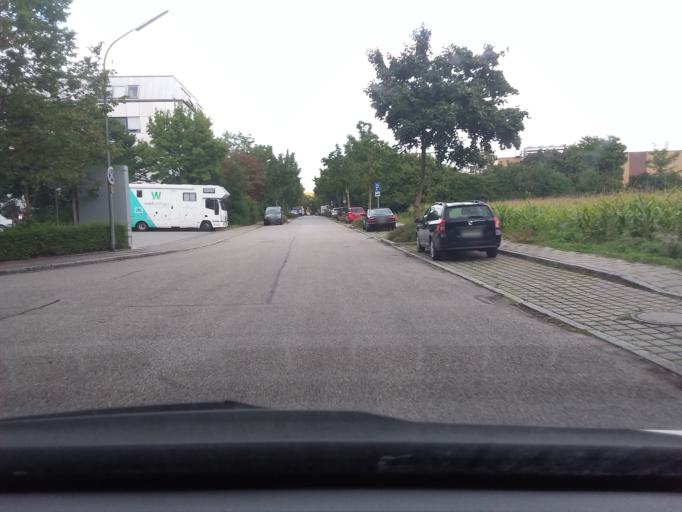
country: DE
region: Bavaria
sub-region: Upper Bavaria
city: Unterschleissheim
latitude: 48.2867
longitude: 11.5647
